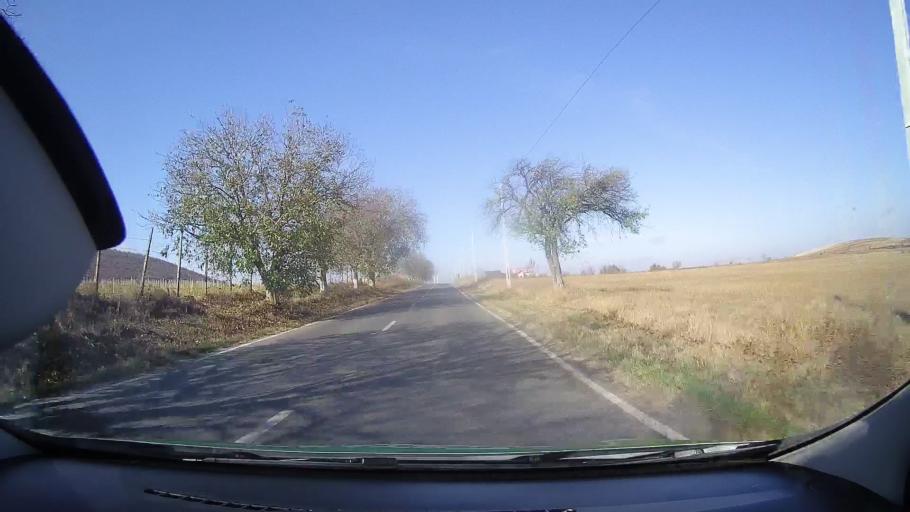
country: RO
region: Tulcea
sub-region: Oras Babadag
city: Babadag
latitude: 44.8829
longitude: 28.7417
